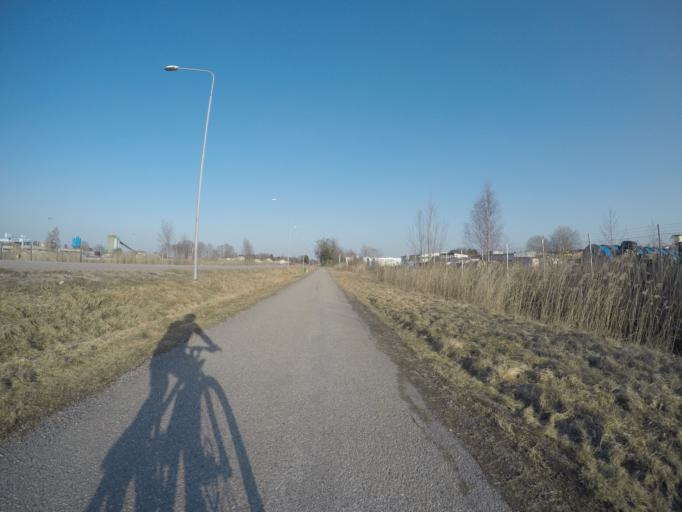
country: SE
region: Vaestmanland
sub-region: Kungsors Kommun
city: Kungsoer
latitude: 59.4242
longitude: 16.1286
